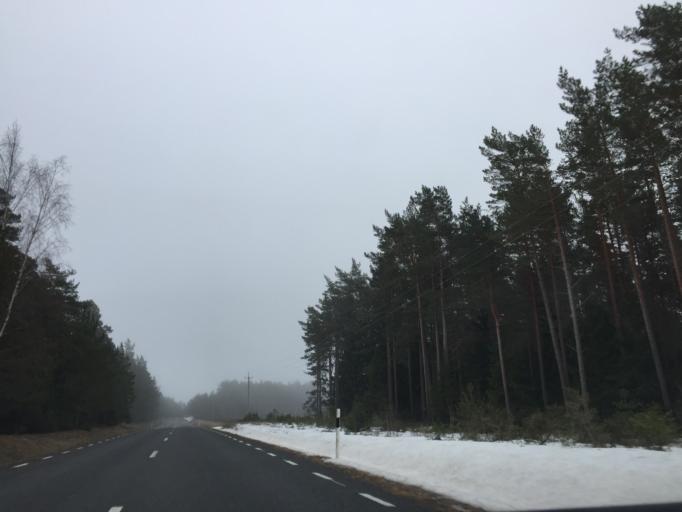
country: EE
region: Saare
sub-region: Kuressaare linn
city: Kuressaare
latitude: 58.4671
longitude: 22.0393
